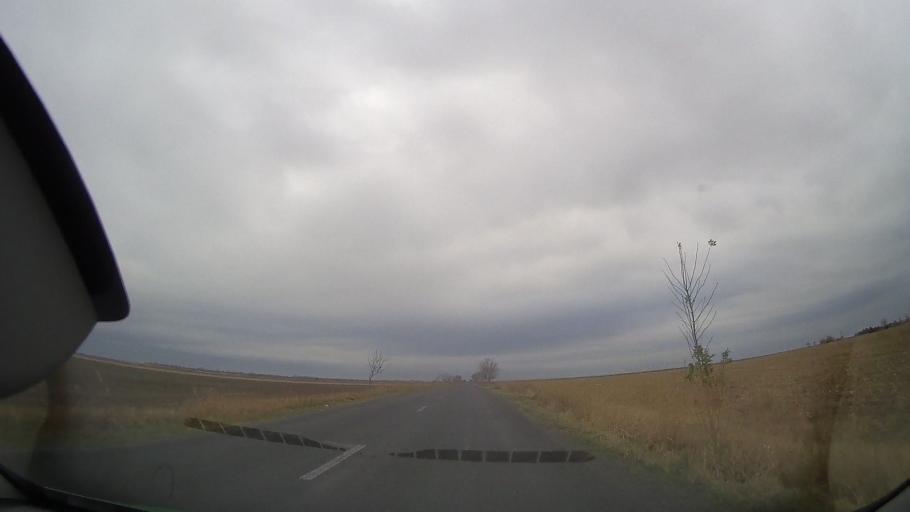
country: RO
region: Buzau
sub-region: Comuna Padina
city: Padina
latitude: 44.7926
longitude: 27.1421
